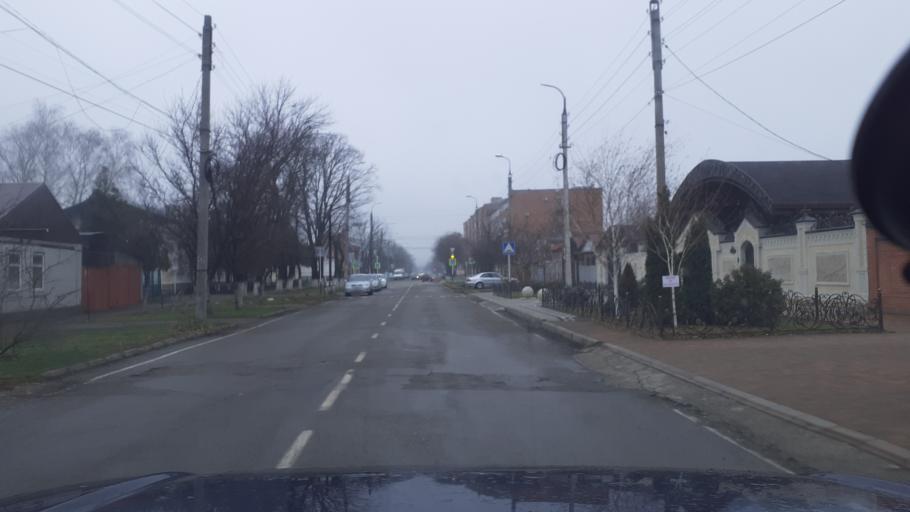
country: RU
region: Adygeya
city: Maykop
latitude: 44.6163
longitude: 40.1113
